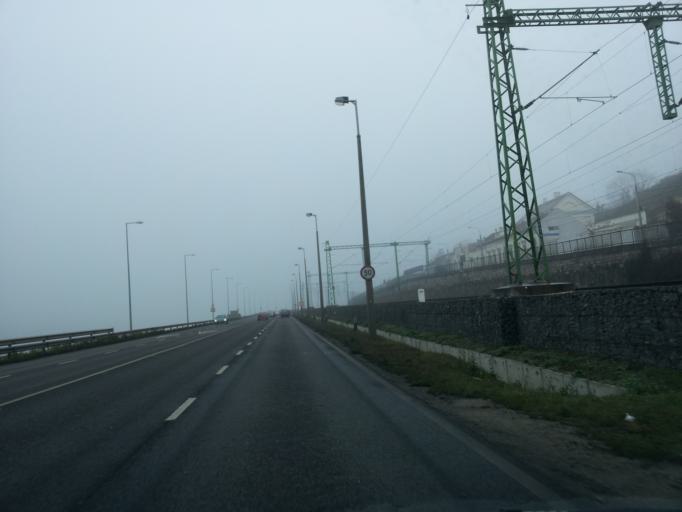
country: HU
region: Budapest
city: Budapest XXII. keruelet
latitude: 47.4203
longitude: 19.0422
